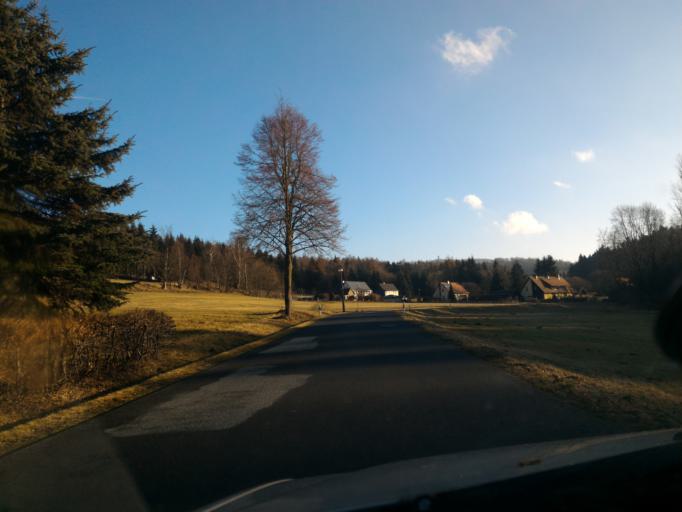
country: DE
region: Saxony
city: Kurort Jonsdorf
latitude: 50.8450
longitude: 14.7059
